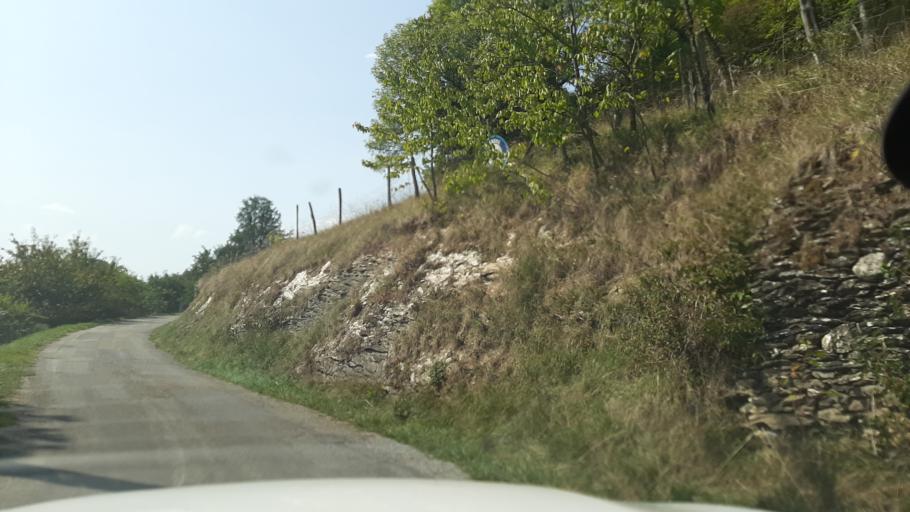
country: FR
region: Rhone-Alpes
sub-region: Departement de la Savoie
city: La Rochette
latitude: 45.4722
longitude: 6.1181
